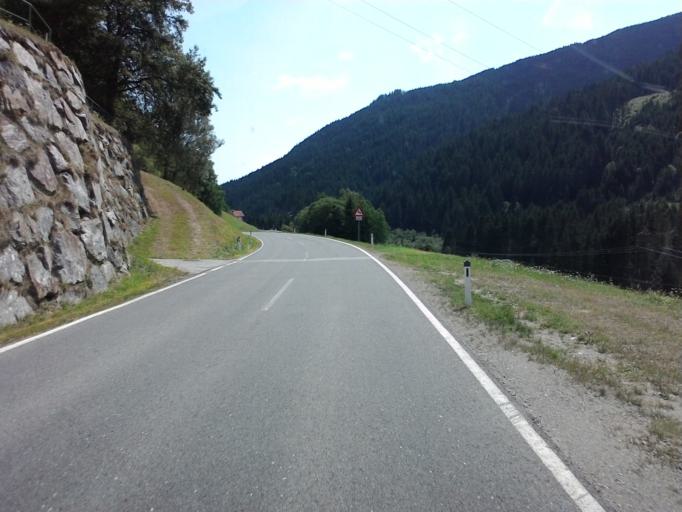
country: AT
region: Tyrol
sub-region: Politischer Bezirk Lienz
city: Untertilliach
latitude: 46.7038
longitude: 12.6827
